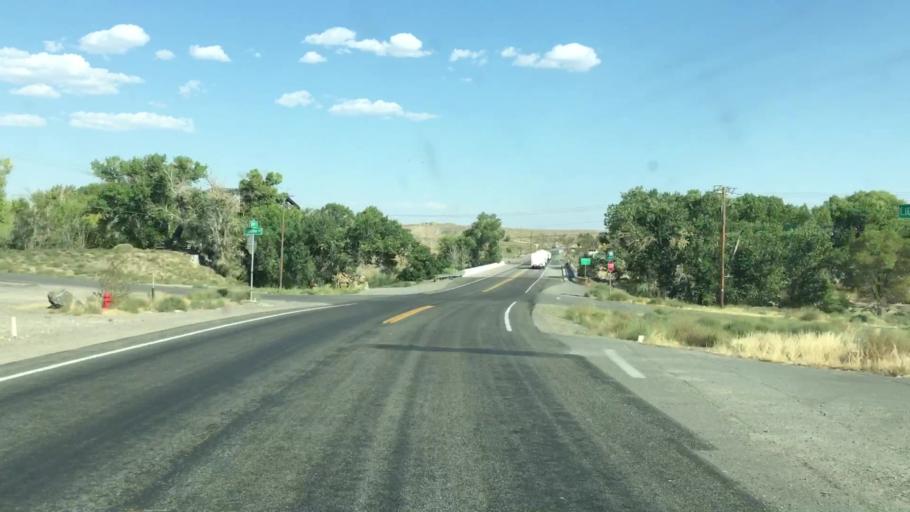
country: US
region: Nevada
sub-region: Lyon County
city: Fernley
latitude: 39.6325
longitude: -119.2848
